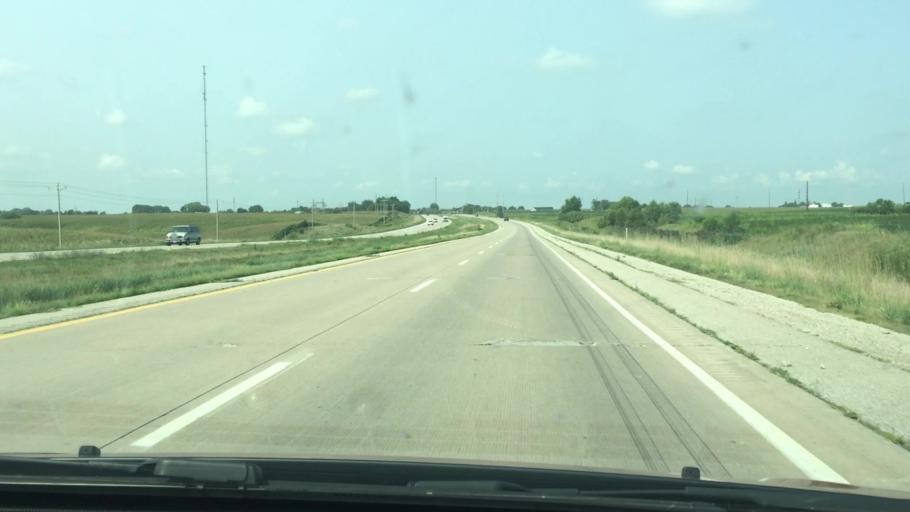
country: US
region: Iowa
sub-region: Cedar County
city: Durant
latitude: 41.5199
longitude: -90.8726
